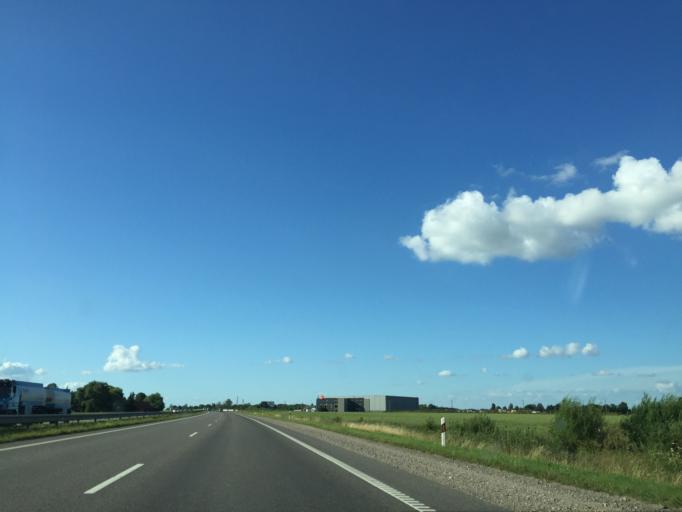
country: LT
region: Kauno apskritis
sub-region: Kauno rajonas
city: Mastaiciai
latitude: 54.8370
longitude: 23.8511
